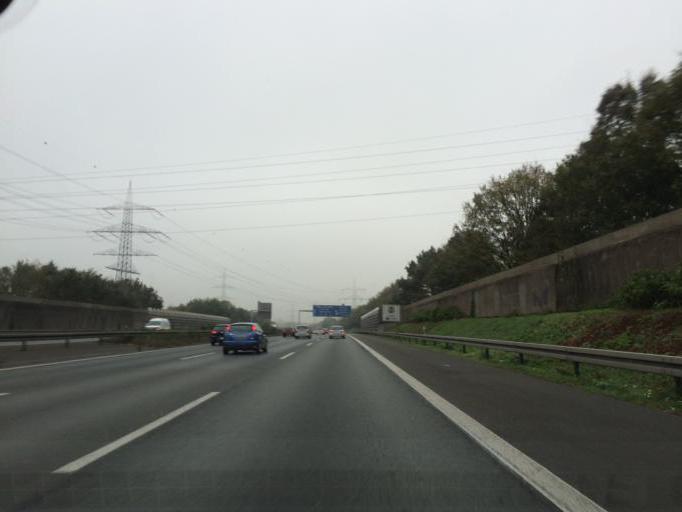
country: DE
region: North Rhine-Westphalia
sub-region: Regierungsbezirk Munster
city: Gladbeck
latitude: 51.5547
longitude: 6.9521
